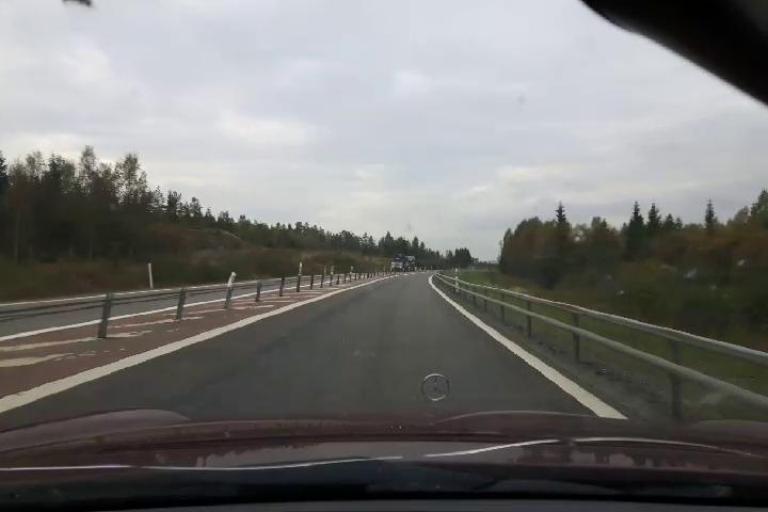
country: SE
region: Vaesternorrland
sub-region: Haernoesands Kommun
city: Haernoesand
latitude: 62.7185
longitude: 17.9138
